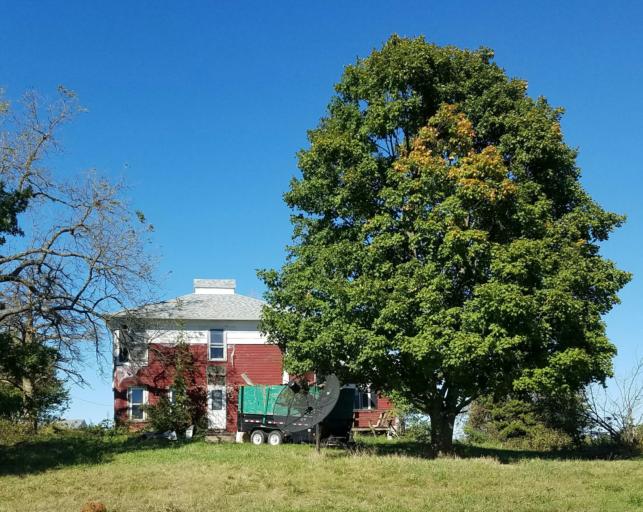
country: US
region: Iowa
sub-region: Decatur County
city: Lamoni
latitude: 40.6238
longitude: -93.9798
